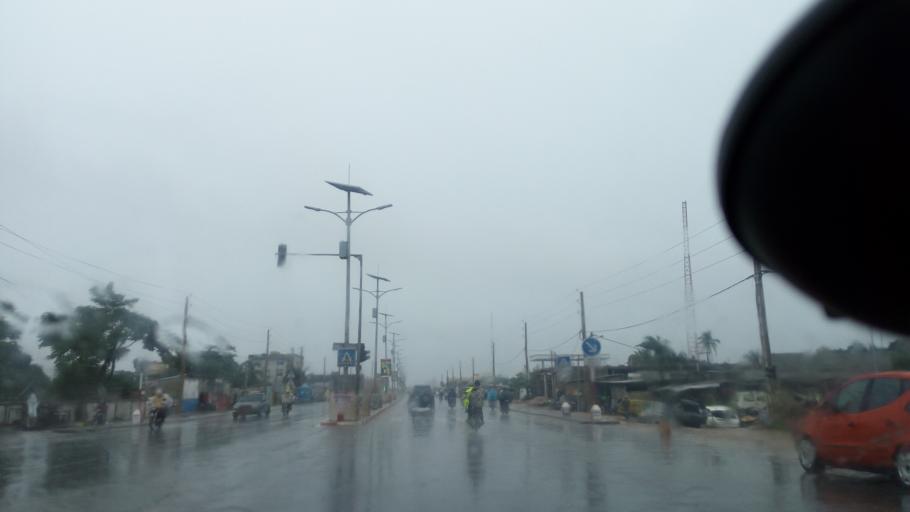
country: BJ
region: Atlantique
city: Abomey-Calavi
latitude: 6.3855
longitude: 2.3291
